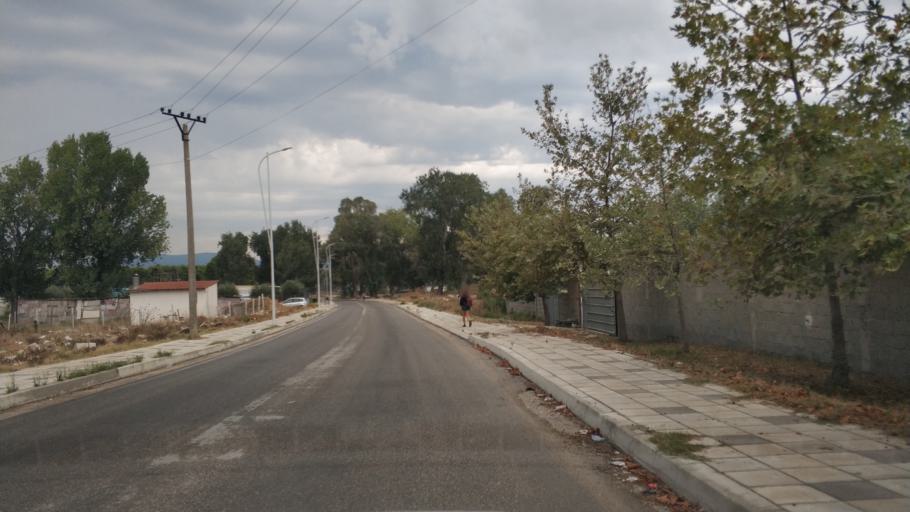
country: AL
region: Vlore
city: Vlore
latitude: 40.4735
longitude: 19.4617
